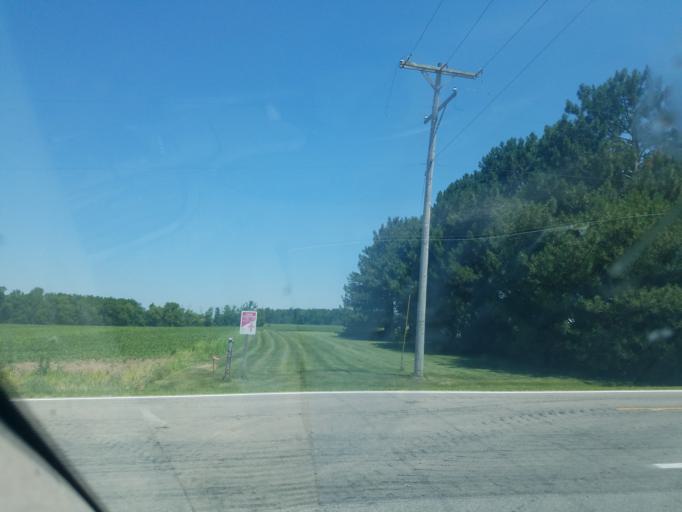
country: US
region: Ohio
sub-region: Mercer County
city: Rockford
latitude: 40.7425
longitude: -84.7370
